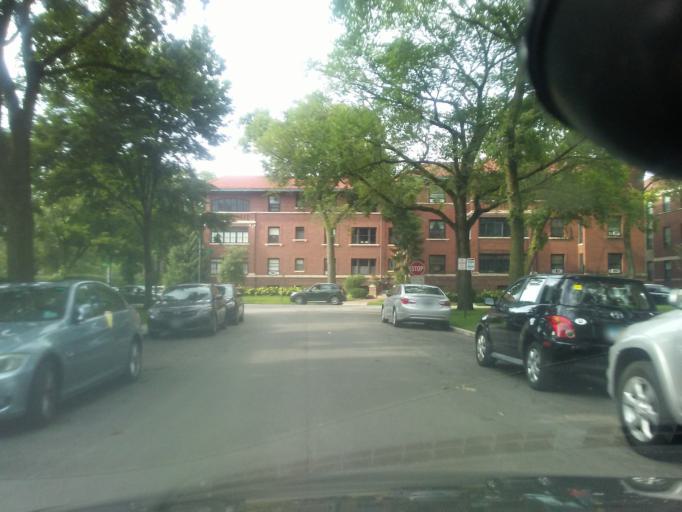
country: US
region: Illinois
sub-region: Cook County
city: Evanston
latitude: 42.0335
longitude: -87.6743
